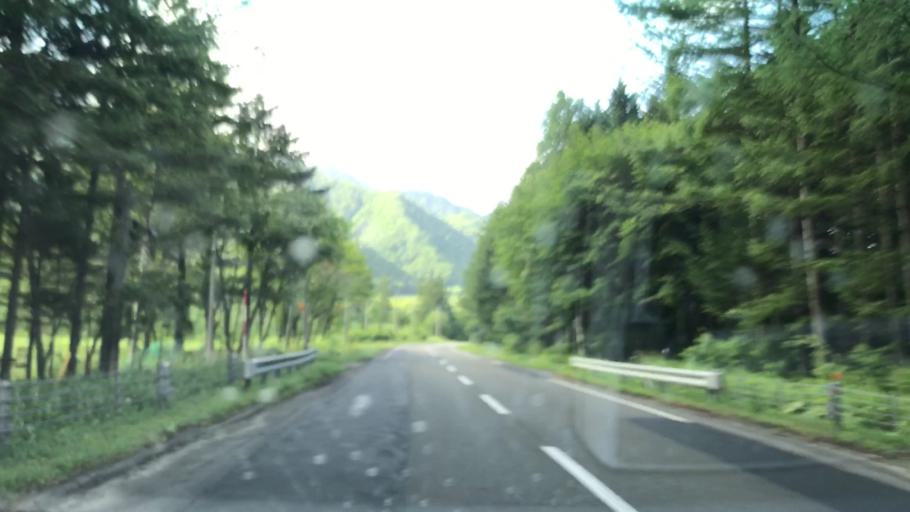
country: JP
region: Hokkaido
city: Shizunai-furukawacho
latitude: 42.8229
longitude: 142.4178
